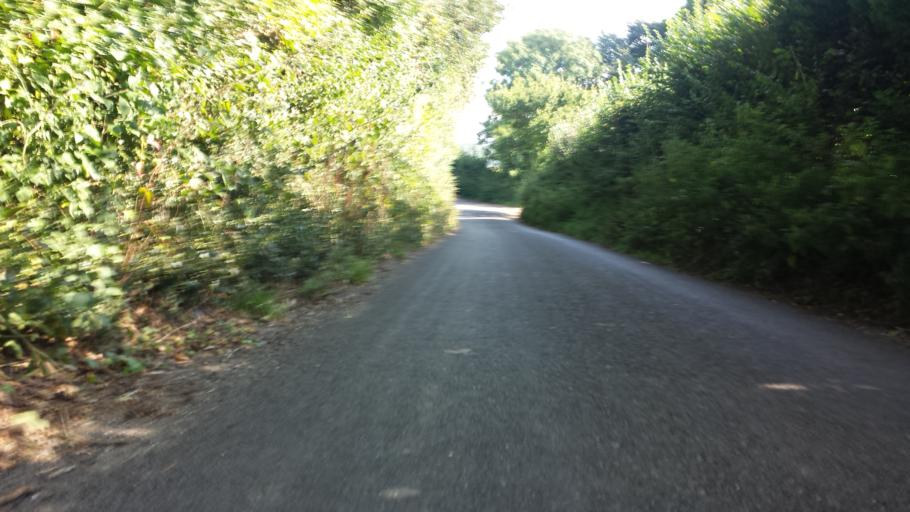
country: GB
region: England
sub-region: Kent
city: Shoreham
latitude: 51.3502
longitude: 0.1769
